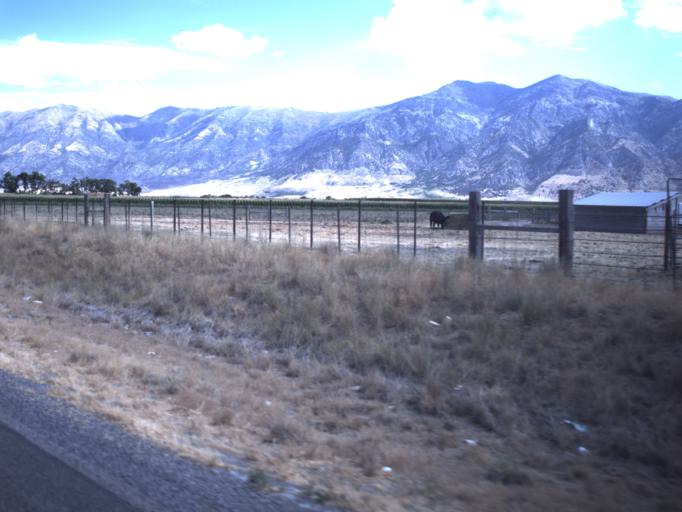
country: US
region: Utah
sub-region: Box Elder County
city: Honeyville
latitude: 41.5920
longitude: -112.1295
